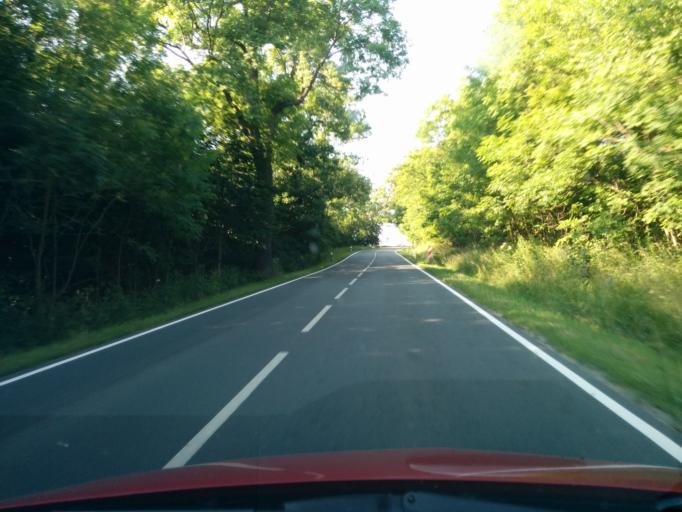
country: DE
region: Saxony-Anhalt
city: Elbingerode
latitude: 51.7764
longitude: 10.8081
